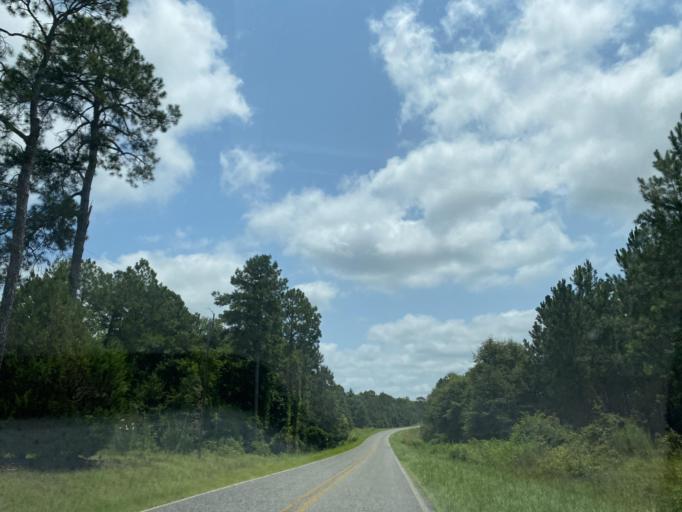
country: US
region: Georgia
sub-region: Wheeler County
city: Alamo
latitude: 32.0755
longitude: -82.7359
